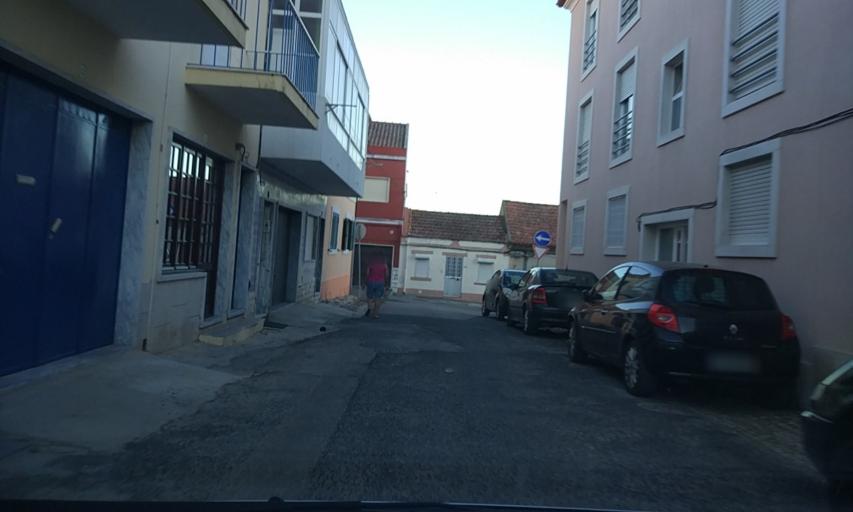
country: PT
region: Setubal
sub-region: Setubal
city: Setubal
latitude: 38.5389
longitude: -8.8809
